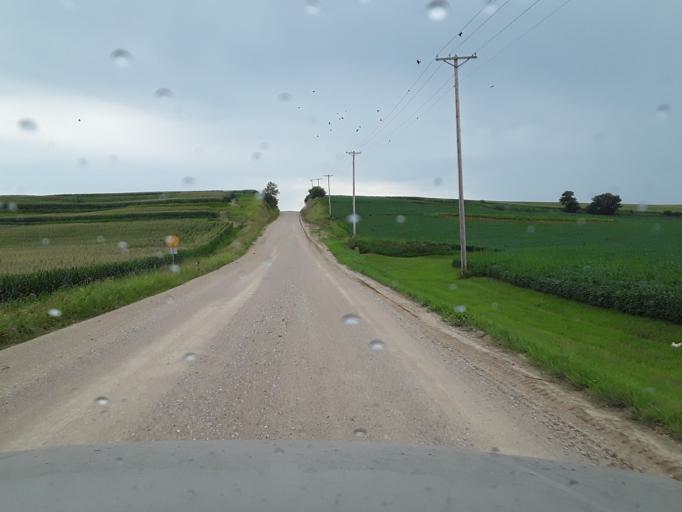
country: US
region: Nebraska
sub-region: Washington County
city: Blair
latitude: 41.5092
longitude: -96.1752
